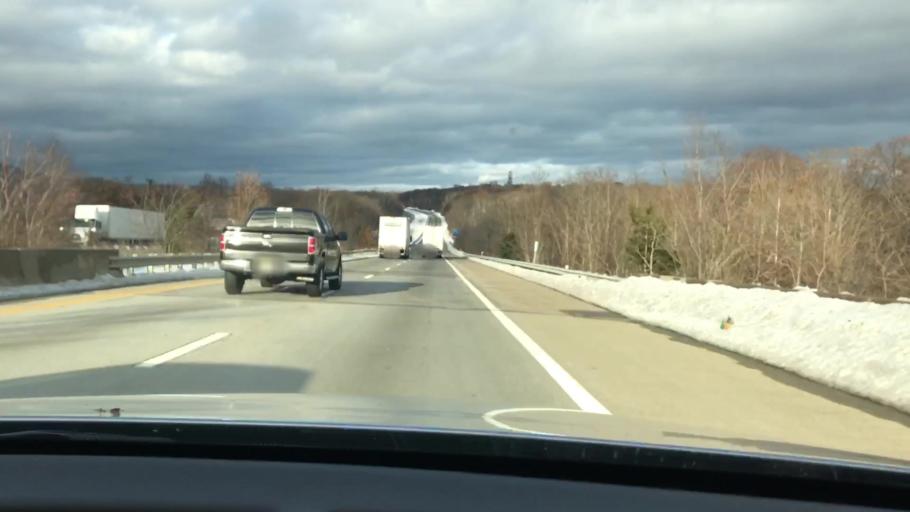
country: US
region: New Jersey
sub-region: Bergen County
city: Ramsey
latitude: 41.0691
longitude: -74.1782
